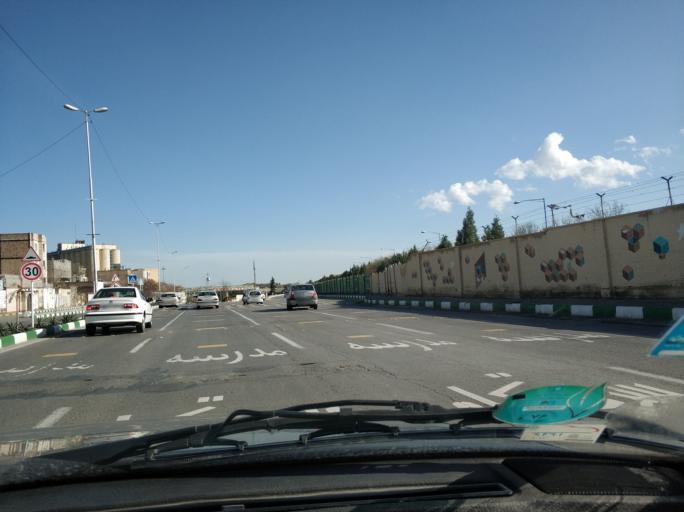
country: IR
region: Razavi Khorasan
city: Mashhad
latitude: 36.3079
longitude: 59.6259
